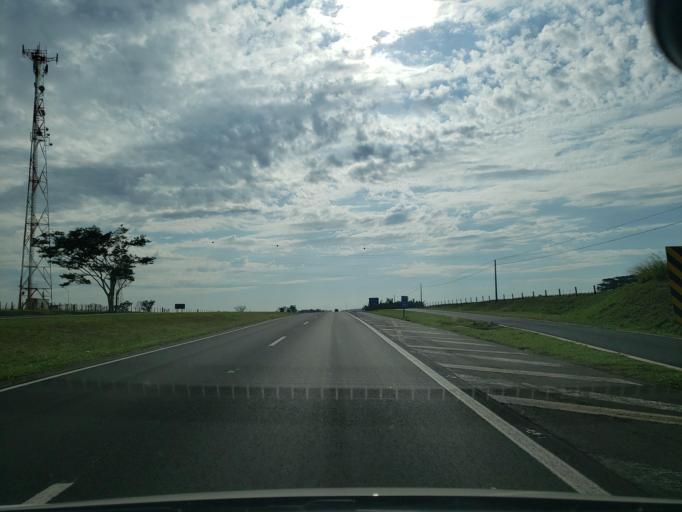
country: BR
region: Sao Paulo
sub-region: Birigui
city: Birigui
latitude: -21.3391
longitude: -50.3253
